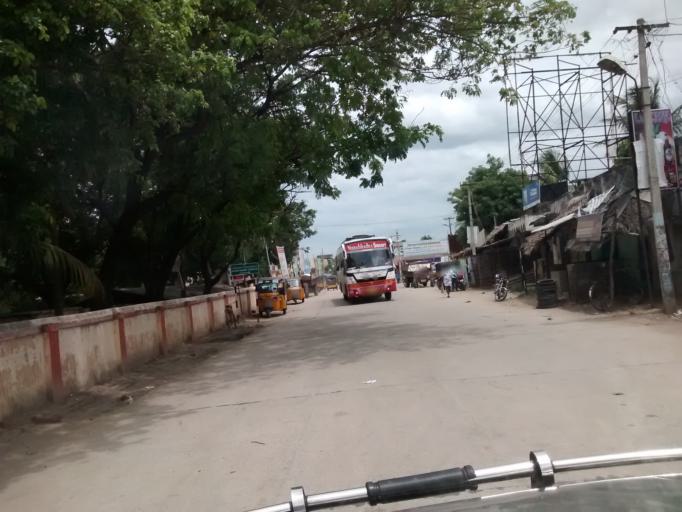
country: IN
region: Andhra Pradesh
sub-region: Chittoor
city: Chittoor
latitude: 13.2777
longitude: 79.0419
